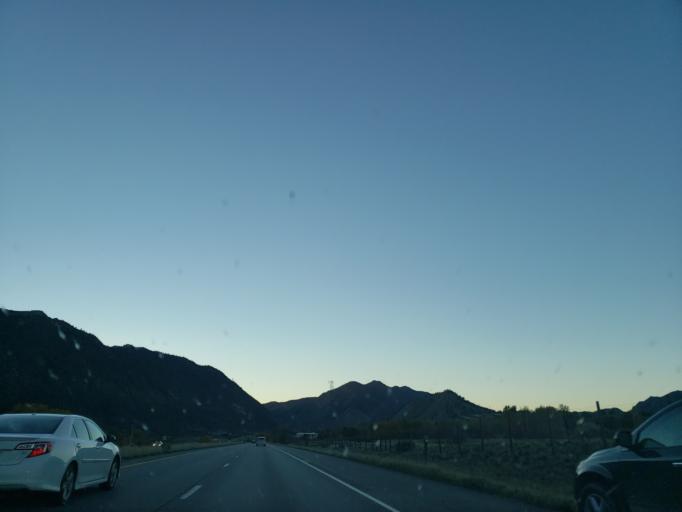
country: US
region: Colorado
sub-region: Garfield County
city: New Castle
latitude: 39.5661
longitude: -107.5033
